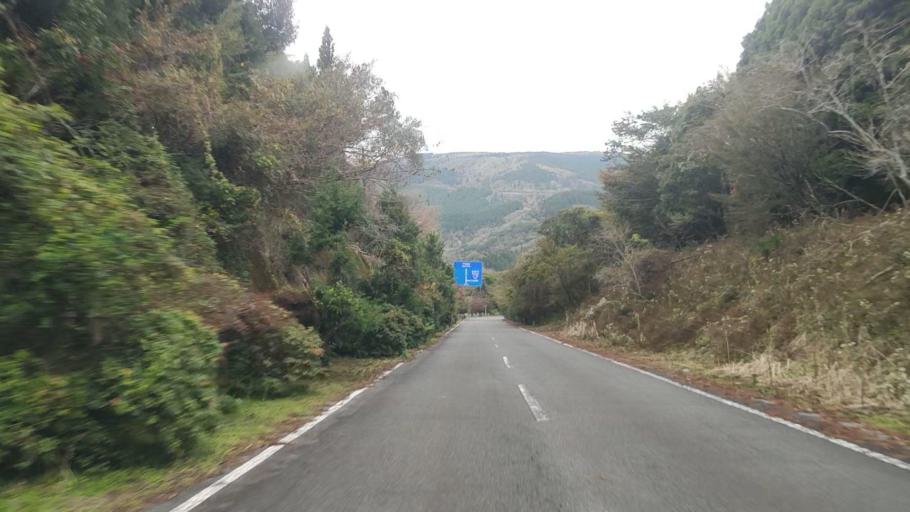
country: JP
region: Shizuoka
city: Heda
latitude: 34.9178
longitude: 138.8421
